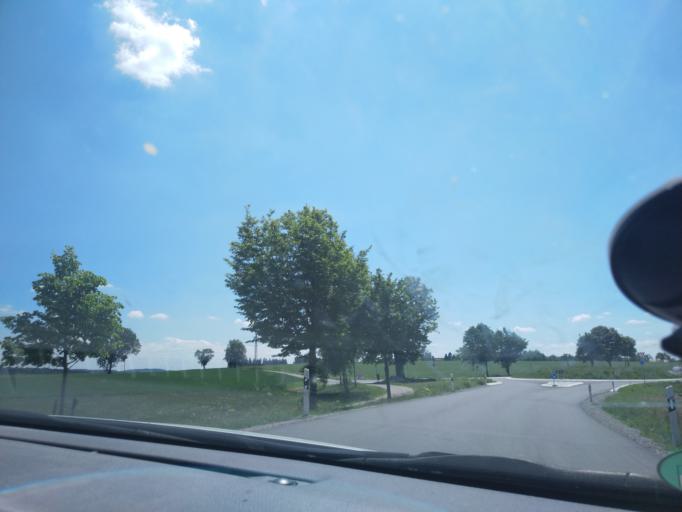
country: DE
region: Baden-Wuerttemberg
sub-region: Freiburg Region
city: Dornhan
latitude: 48.3307
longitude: 8.4688
